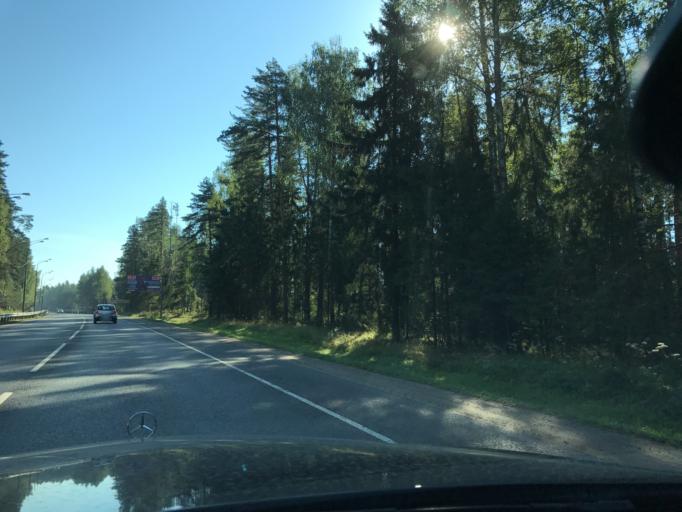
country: RU
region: Moskovskaya
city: Chernogolovka
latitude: 55.9814
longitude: 38.3258
